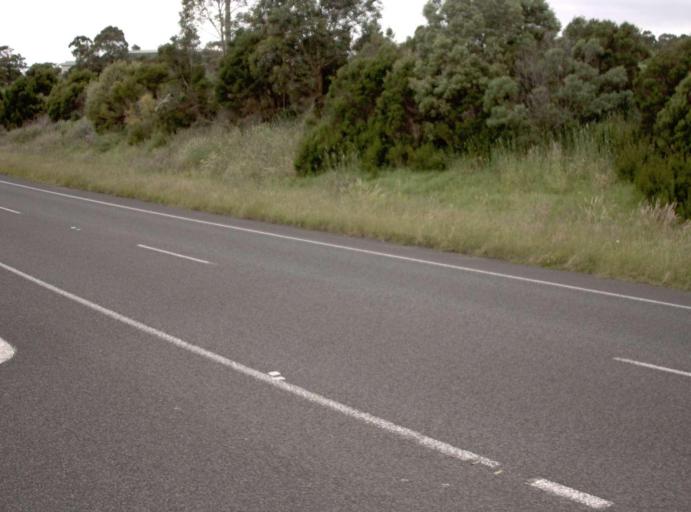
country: AU
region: Victoria
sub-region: Bass Coast
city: North Wonthaggi
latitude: -38.3663
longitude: 145.6933
